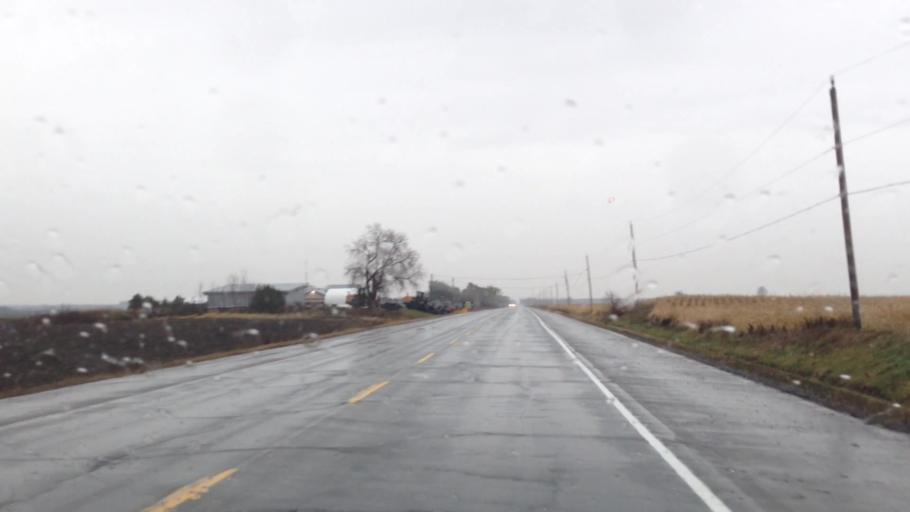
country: CA
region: Ontario
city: Clarence-Rockland
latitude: 45.4640
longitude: -75.4316
